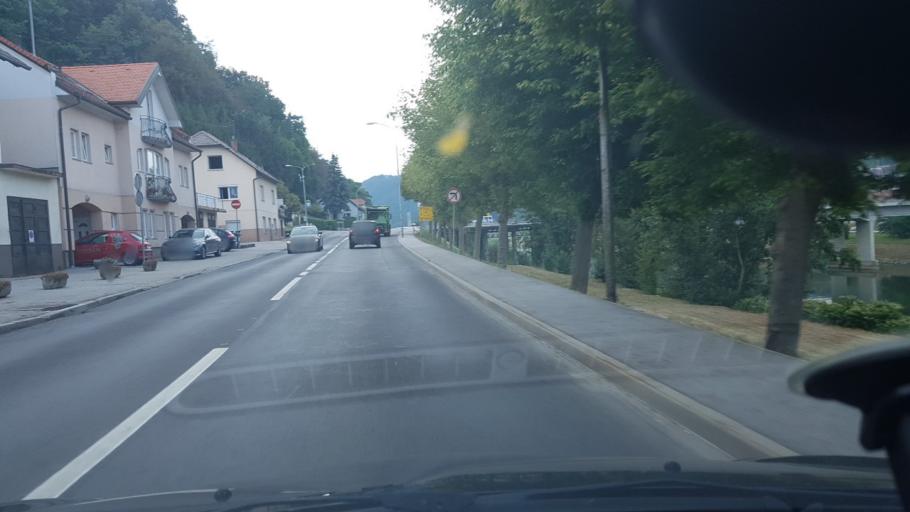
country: SI
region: Krsko
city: Krsko
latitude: 45.9554
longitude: 15.4864
